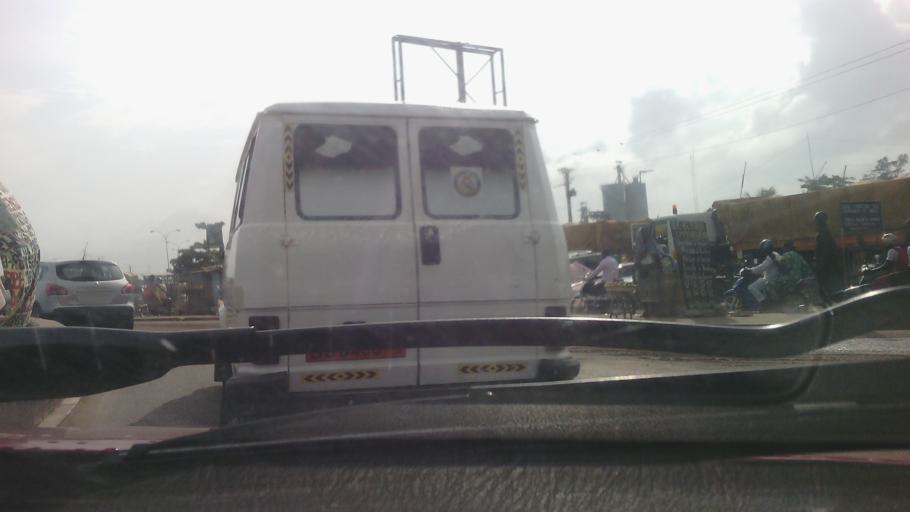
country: BJ
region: Littoral
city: Cotonou
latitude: 6.3703
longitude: 2.5075
